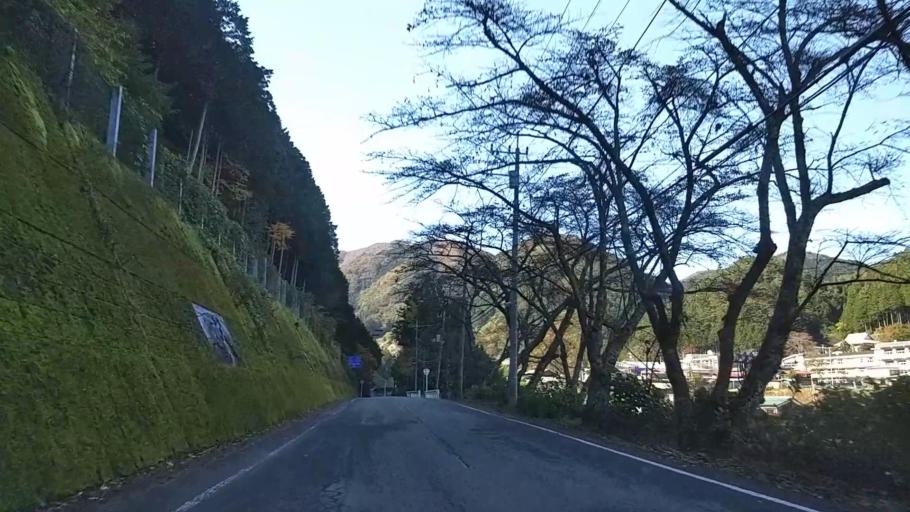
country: JP
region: Yamanashi
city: Otsuki
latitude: 35.7580
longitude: 138.9430
